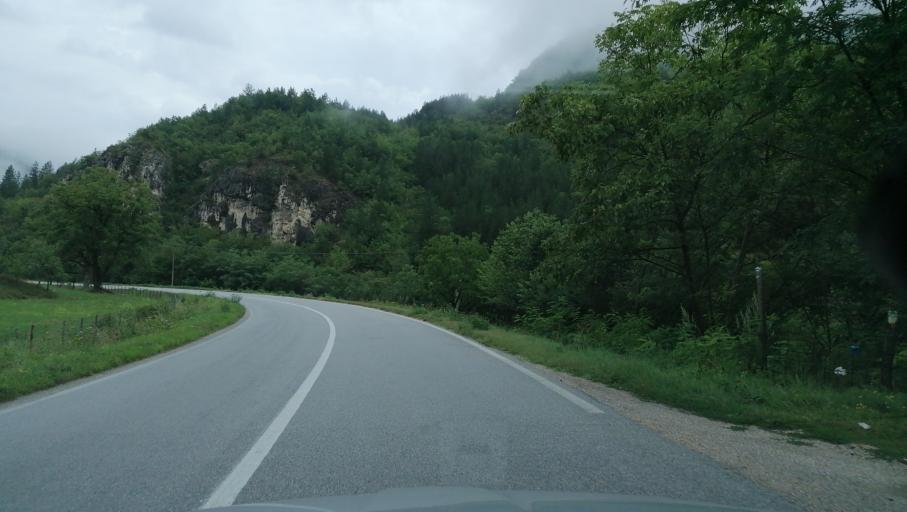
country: RS
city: Durici
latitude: 43.7560
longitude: 19.3965
